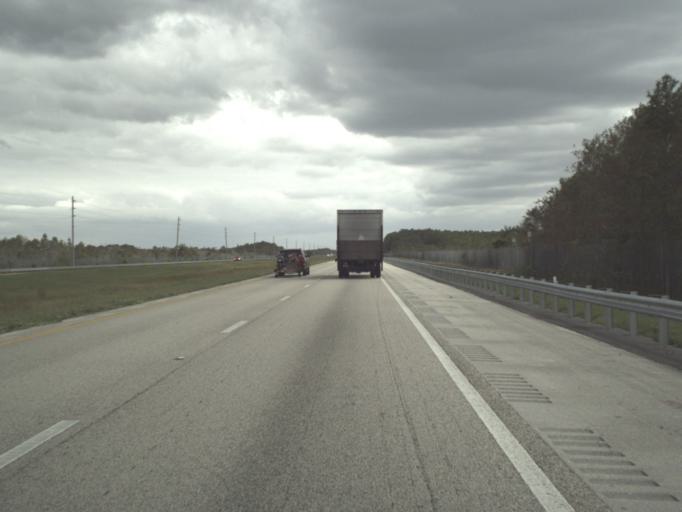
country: US
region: Florida
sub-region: Collier County
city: Immokalee
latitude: 26.1675
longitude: -81.1478
